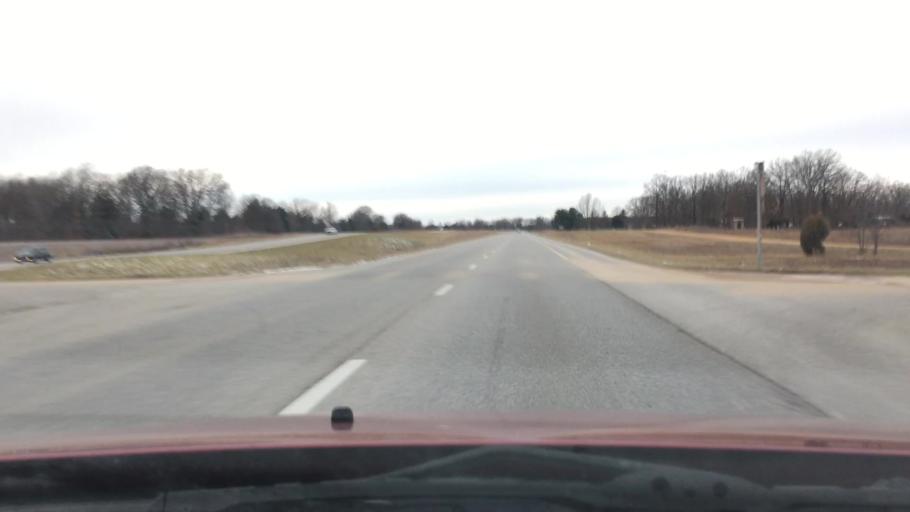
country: US
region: Missouri
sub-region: Webster County
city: Seymour
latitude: 37.1628
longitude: -92.7969
